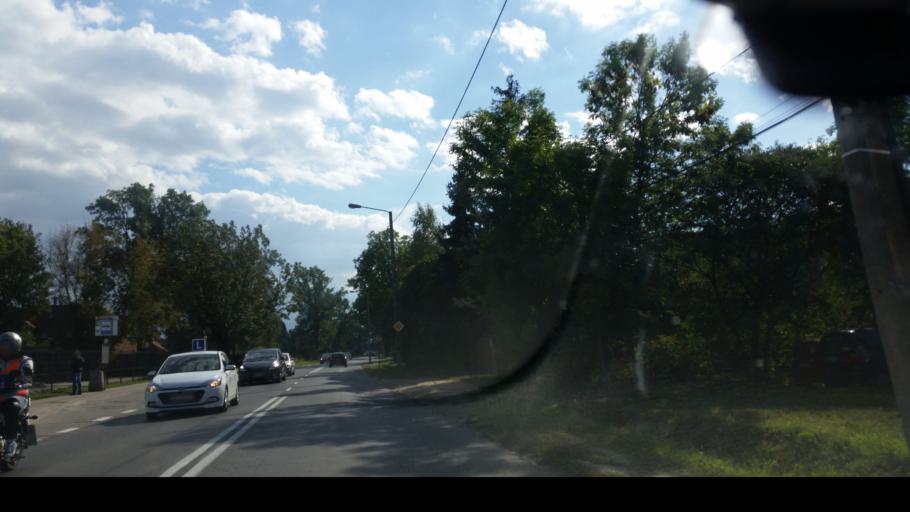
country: PL
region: Masovian Voivodeship
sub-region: Warszawa
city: Targowek
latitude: 52.3156
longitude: 21.0297
